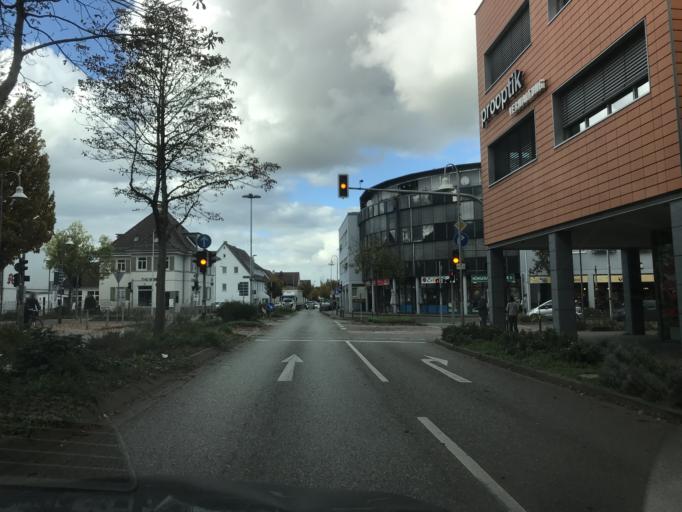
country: DE
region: Baden-Wuerttemberg
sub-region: Regierungsbezirk Stuttgart
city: Wendlingen am Neckar
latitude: 48.6724
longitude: 9.3799
